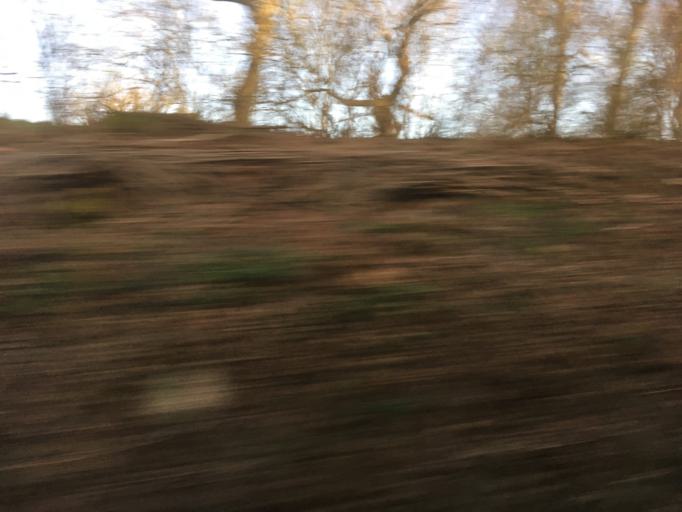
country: GB
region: England
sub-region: Wiltshire
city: Malmesbury
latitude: 51.5419
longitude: -2.1138
